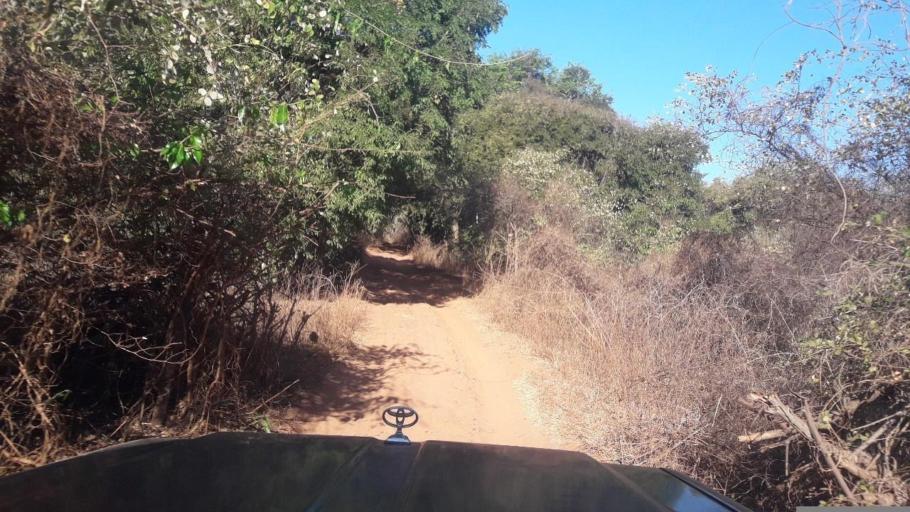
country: MG
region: Boeny
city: Sitampiky
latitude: -16.4197
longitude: 45.6170
